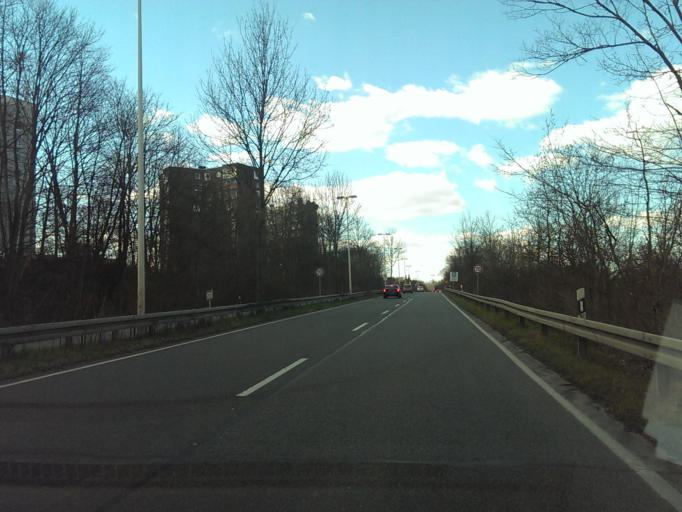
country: DE
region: Lower Saxony
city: Hildesheim
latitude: 52.1351
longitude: 9.9461
